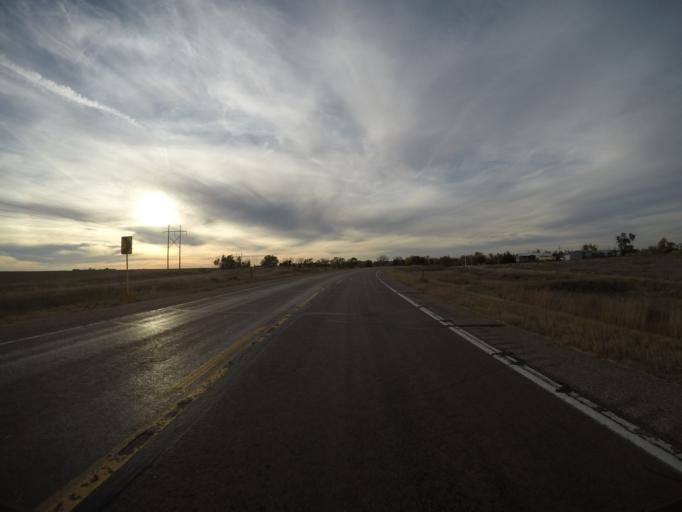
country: US
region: Colorado
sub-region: Yuma County
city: Yuma
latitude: 39.6554
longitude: -102.8420
